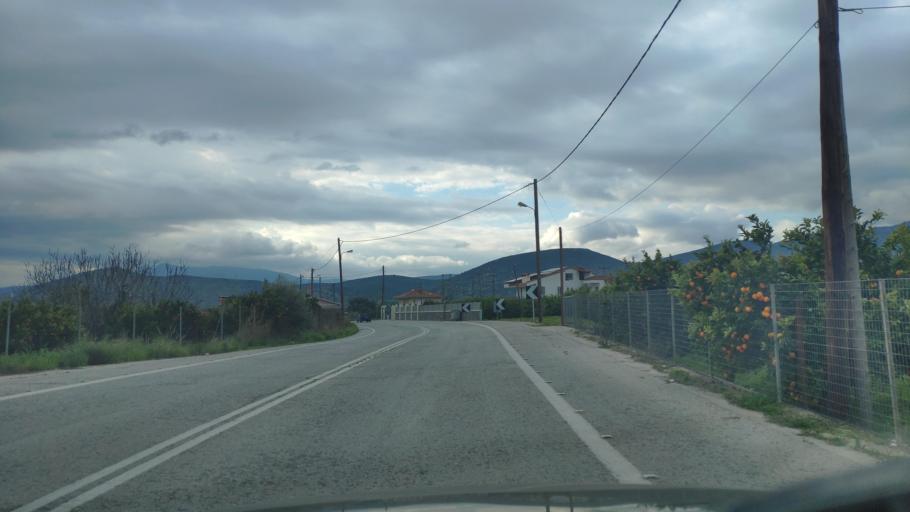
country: GR
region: Peloponnese
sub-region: Nomos Argolidos
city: Nea Kios
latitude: 37.5782
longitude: 22.7090
